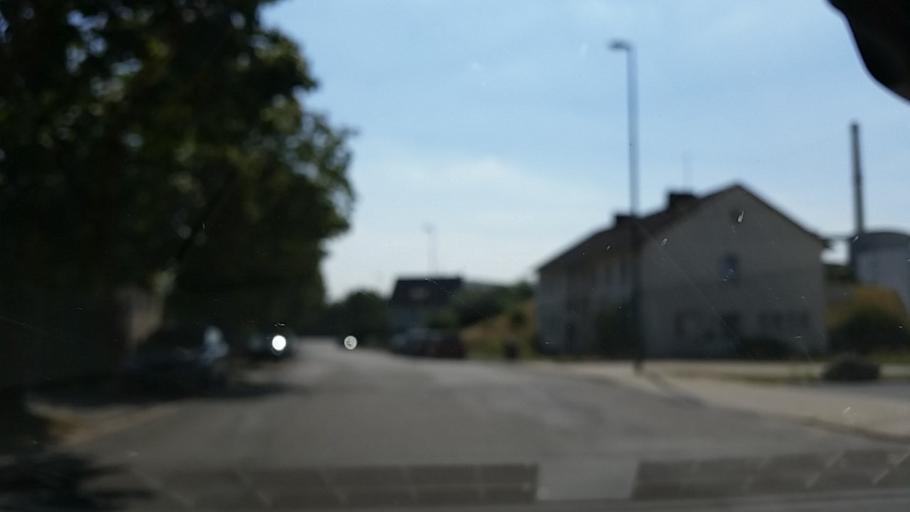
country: DE
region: Lower Saxony
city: Uelzen
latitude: 52.9817
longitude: 10.5564
